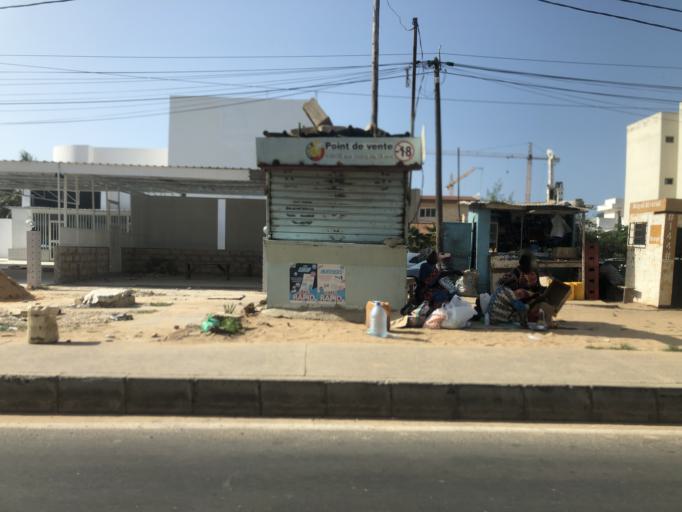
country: SN
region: Dakar
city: Mermoz Boabab
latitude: 14.7503
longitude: -17.5042
